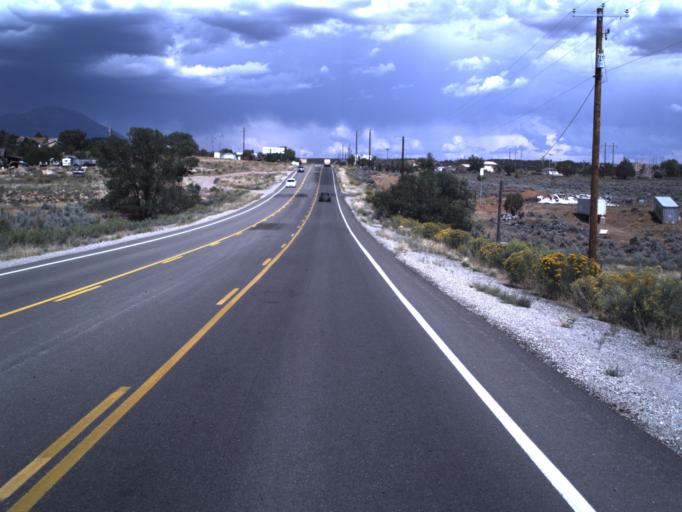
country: US
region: Utah
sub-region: San Juan County
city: Blanding
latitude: 37.6369
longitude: -109.4658
